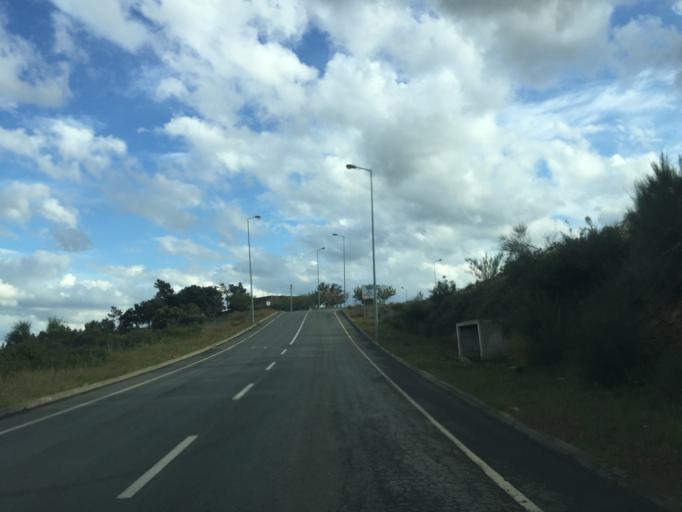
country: PT
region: Braganca
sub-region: Alfandega da Fe
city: Alfandega da Fe
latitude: 41.3383
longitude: -6.9600
